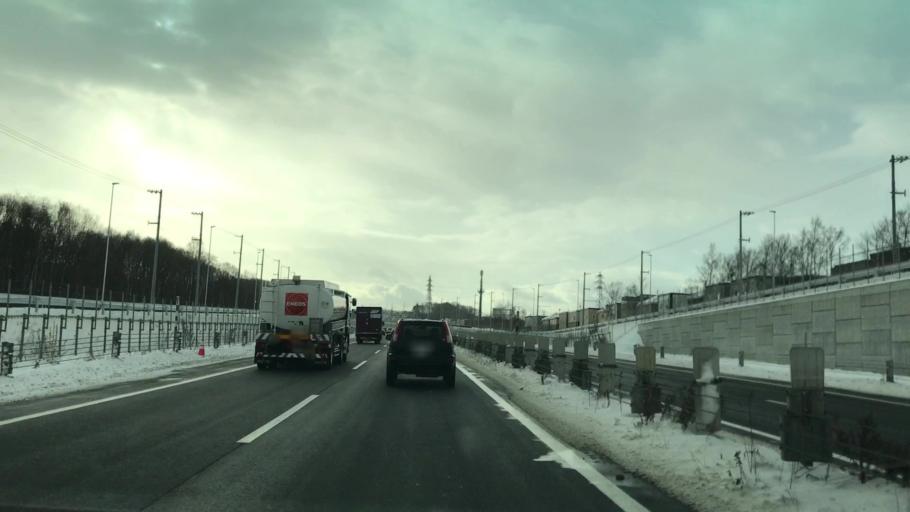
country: JP
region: Hokkaido
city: Kitahiroshima
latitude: 42.9901
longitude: 141.4699
